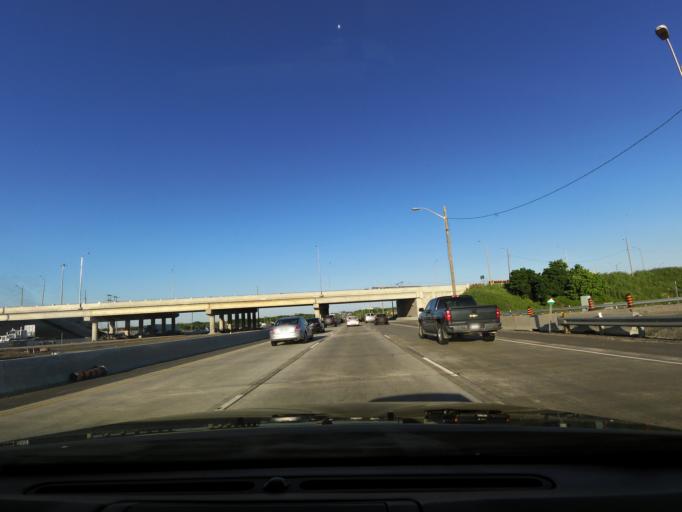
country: CA
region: Ontario
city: Mississauga
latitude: 43.6213
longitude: -79.7069
